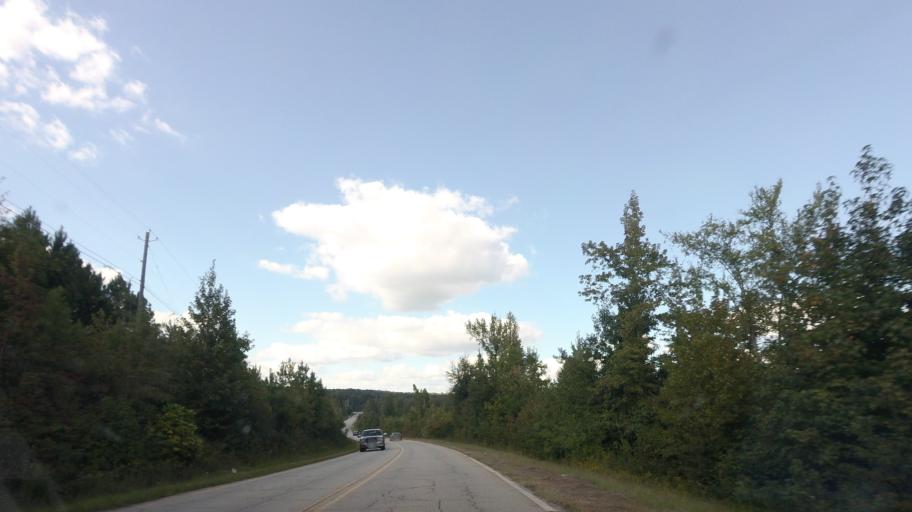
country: US
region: Georgia
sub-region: Lamar County
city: Barnesville
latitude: 33.0808
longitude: -84.1545
